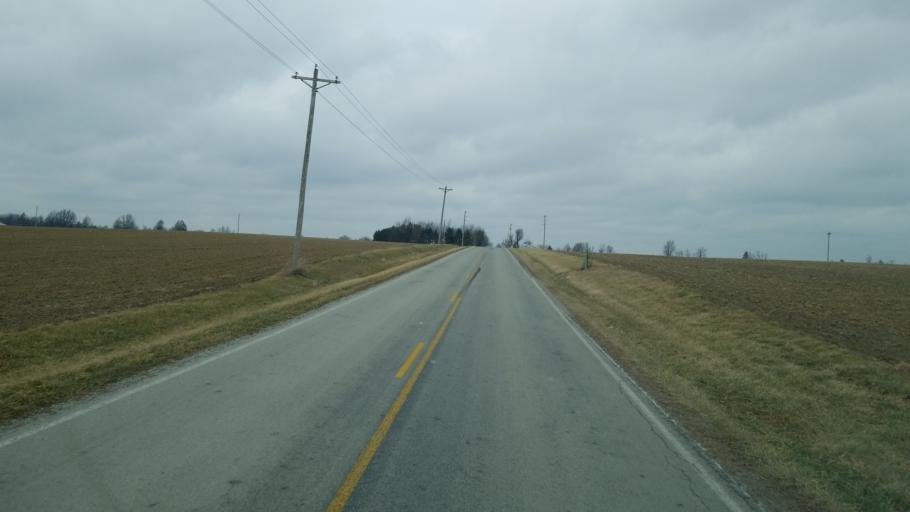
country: US
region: Ohio
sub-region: Hardin County
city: Forest
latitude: 40.7864
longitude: -83.4194
